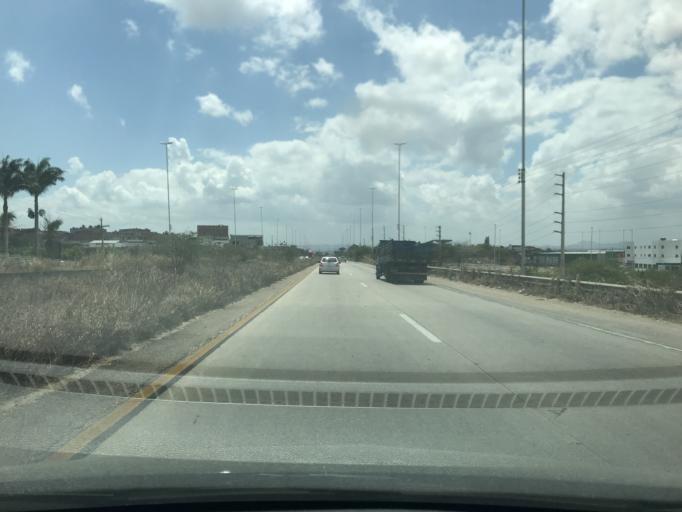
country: BR
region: Pernambuco
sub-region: Caruaru
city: Caruaru
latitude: -8.3044
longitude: -35.9703
